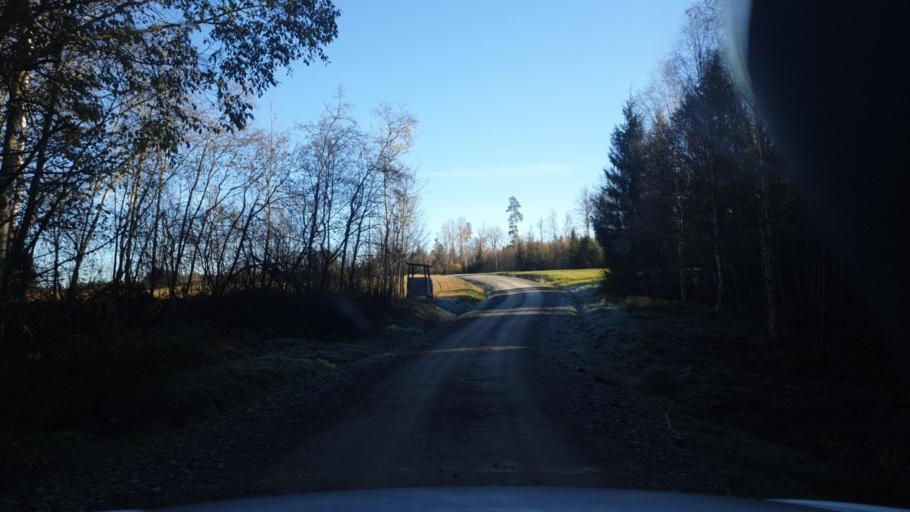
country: SE
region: Vaermland
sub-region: Karlstads Kommun
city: Edsvalla
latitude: 59.4832
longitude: 13.1466
